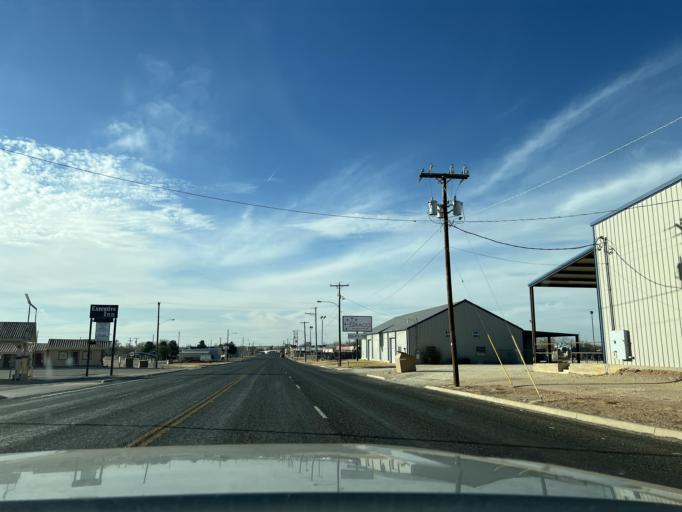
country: US
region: Texas
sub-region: Scurry County
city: Snyder
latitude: 32.7149
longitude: -100.8985
